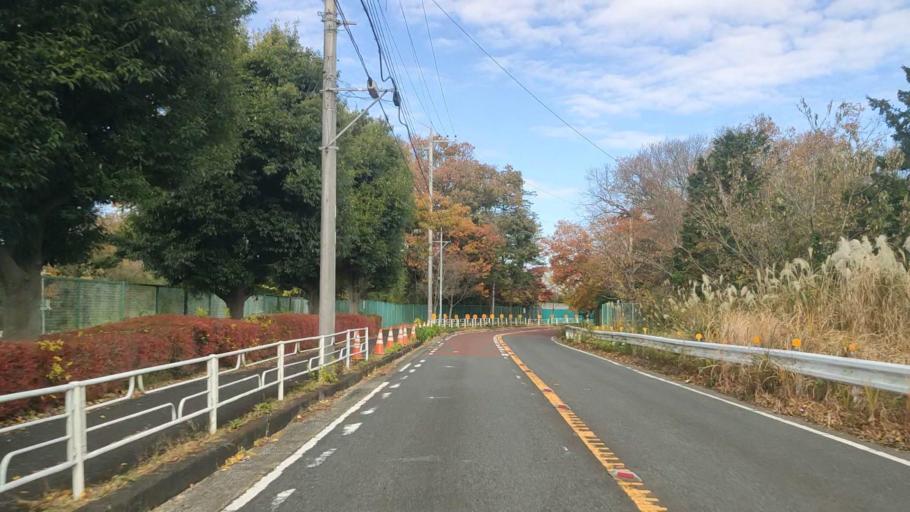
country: JP
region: Kanagawa
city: Minami-rinkan
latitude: 35.4469
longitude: 139.5374
